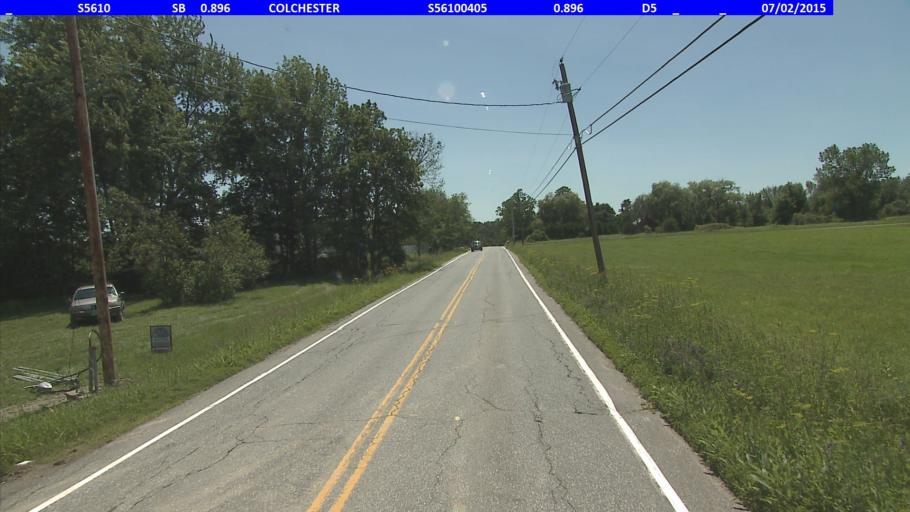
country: US
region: Vermont
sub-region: Chittenden County
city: Colchester
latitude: 44.5545
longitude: -73.1387
